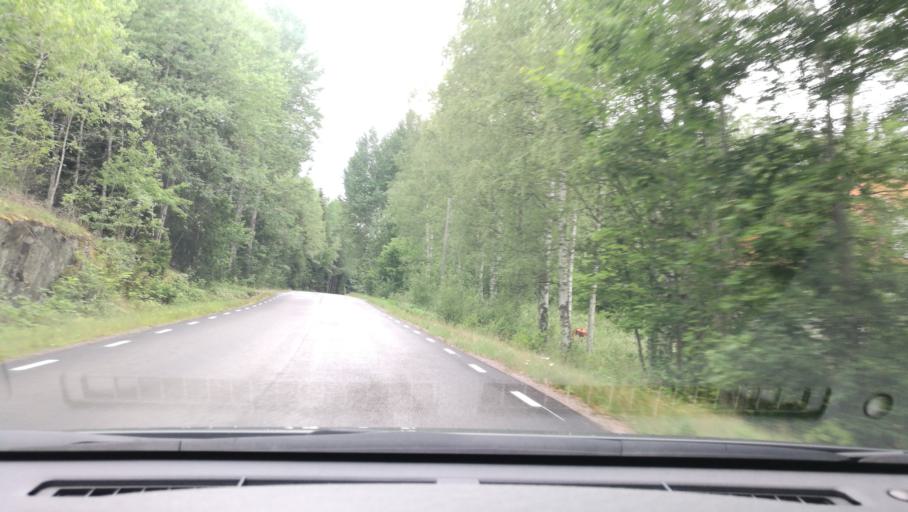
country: SE
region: OEstergoetland
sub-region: Norrkopings Kommun
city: Svartinge
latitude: 58.8197
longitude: 16.0128
